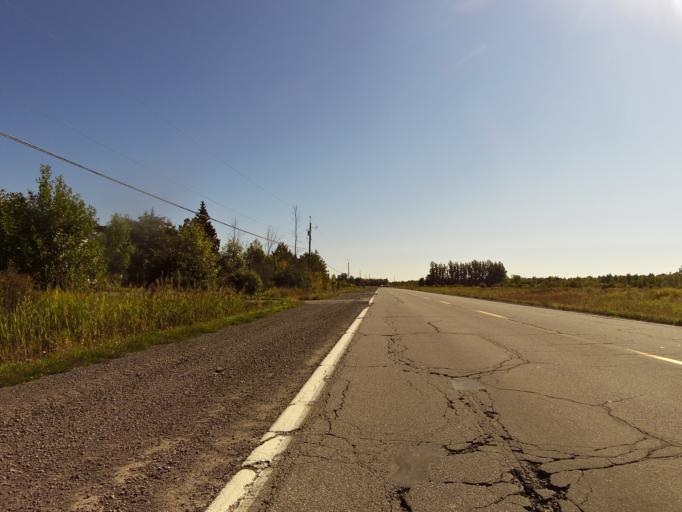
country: CA
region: Ontario
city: Clarence-Rockland
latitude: 45.3645
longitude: -75.4277
